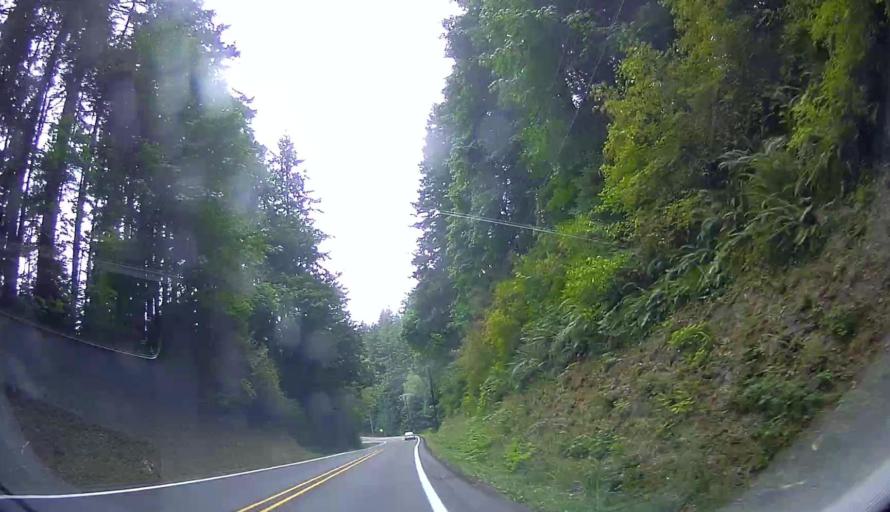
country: US
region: Washington
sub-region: Snohomish County
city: Warm Beach
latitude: 48.1261
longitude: -122.3560
